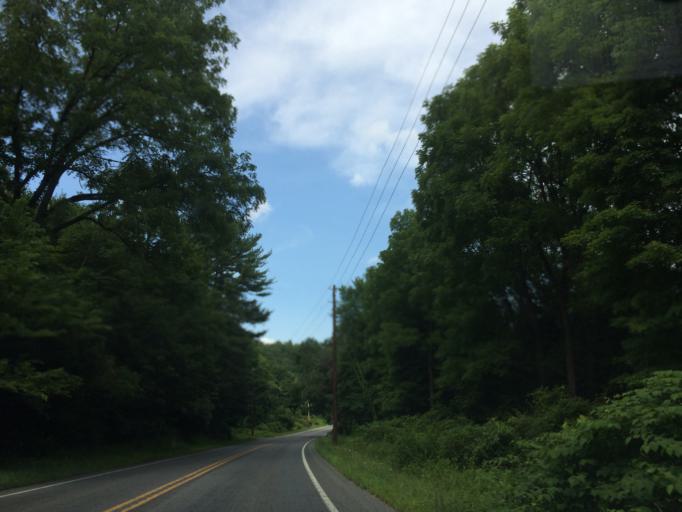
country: US
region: Pennsylvania
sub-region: Pike County
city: Saw Creek
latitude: 41.0951
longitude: -75.0002
